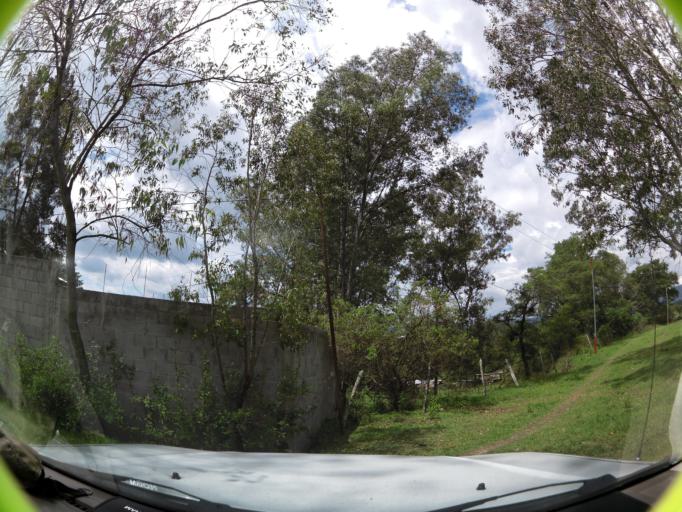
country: GT
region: Huehuetenango
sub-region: Municipio de Huehuetenango
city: Huehuetenango
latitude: 15.3367
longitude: -91.4964
